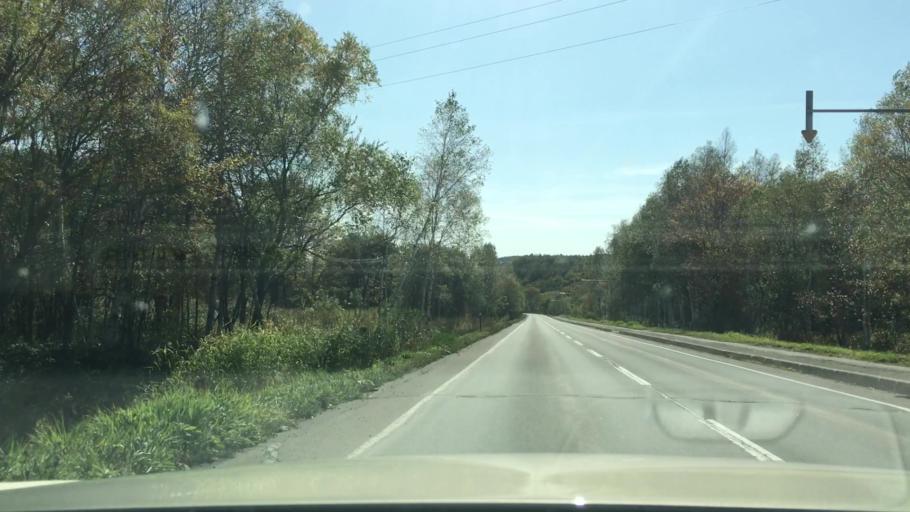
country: JP
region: Hokkaido
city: Kitami
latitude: 43.5836
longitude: 143.6815
